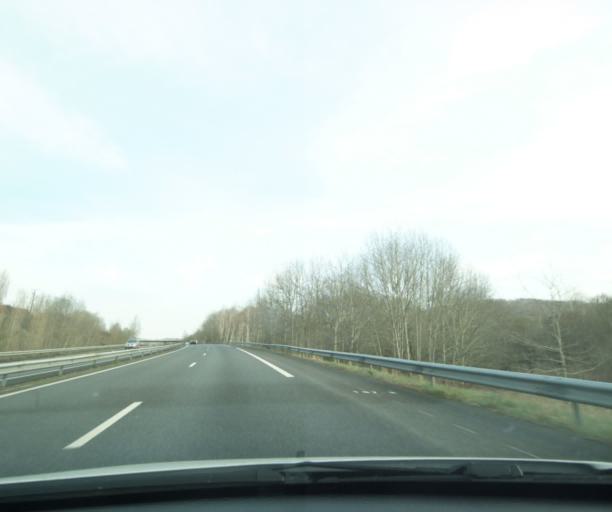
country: FR
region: Midi-Pyrenees
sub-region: Departement des Hautes-Pyrenees
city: Tournay
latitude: 43.1765
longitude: 0.2292
